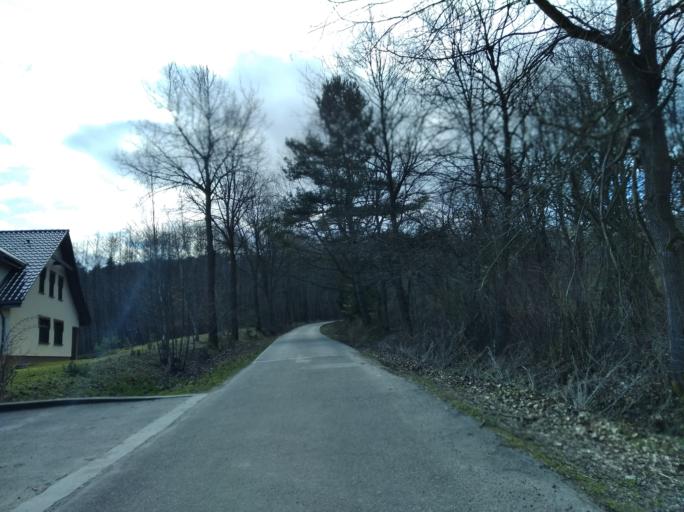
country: PL
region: Subcarpathian Voivodeship
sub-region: Powiat strzyzowski
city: Wysoka Strzyzowska
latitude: 49.8025
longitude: 21.7394
